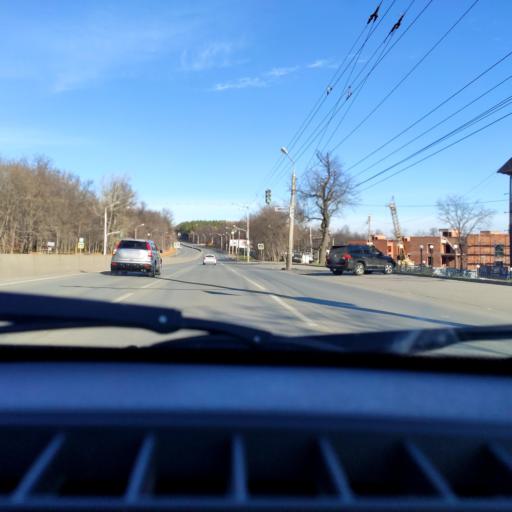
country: RU
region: Bashkortostan
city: Ufa
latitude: 54.7308
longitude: 56.0247
